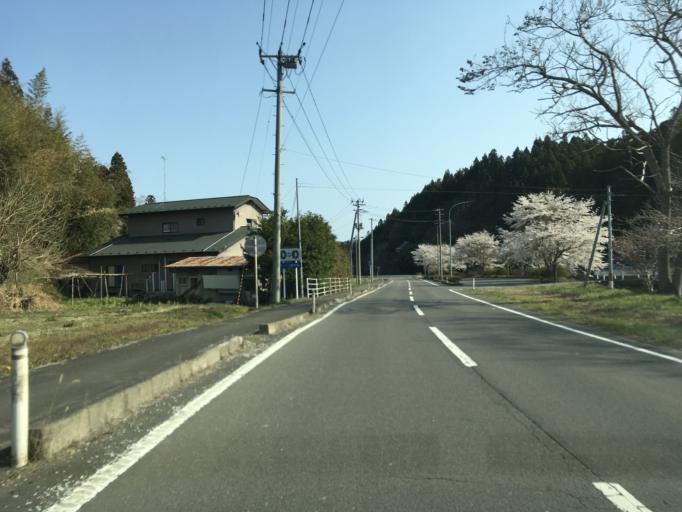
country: JP
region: Iwate
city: Ichinoseki
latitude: 38.7847
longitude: 141.3254
